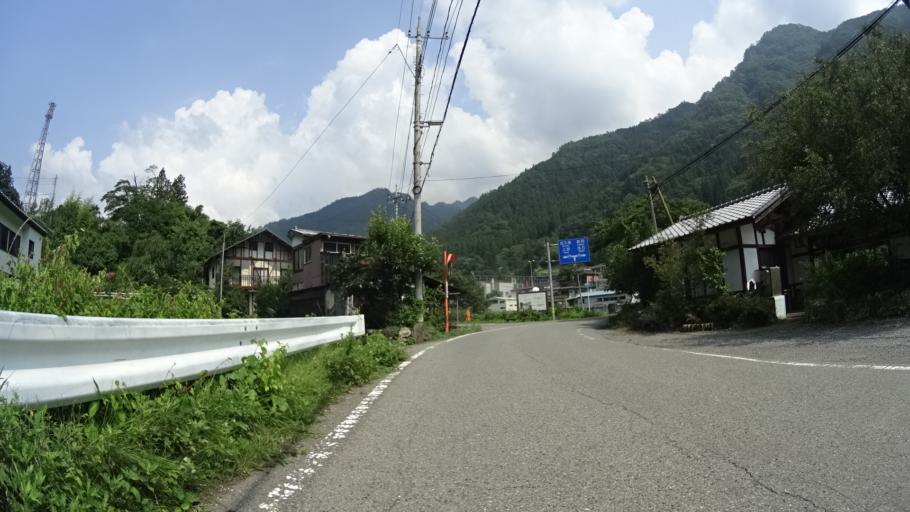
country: JP
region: Gunma
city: Tomioka
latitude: 36.0899
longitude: 138.8291
